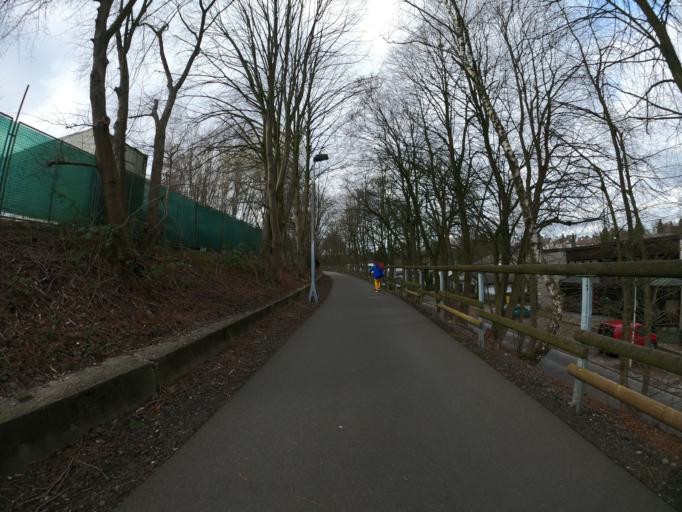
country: DE
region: North Rhine-Westphalia
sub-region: Regierungsbezirk Dusseldorf
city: Solingen
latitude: 51.1776
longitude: 7.0899
